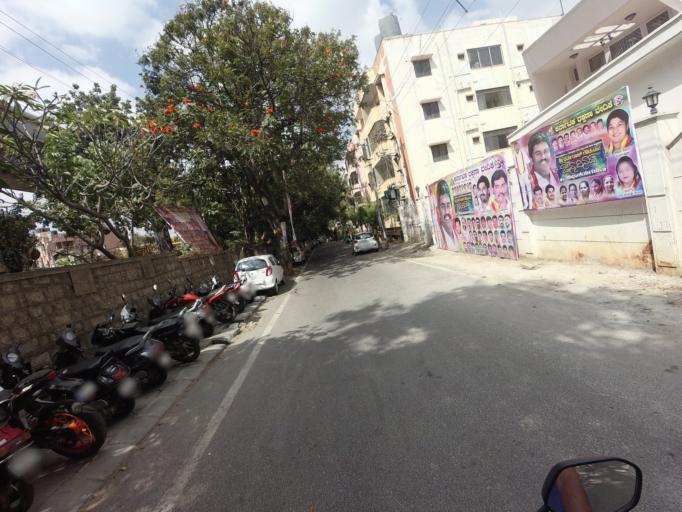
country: IN
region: Karnataka
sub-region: Bangalore Urban
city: Bangalore
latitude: 12.9582
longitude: 77.5340
